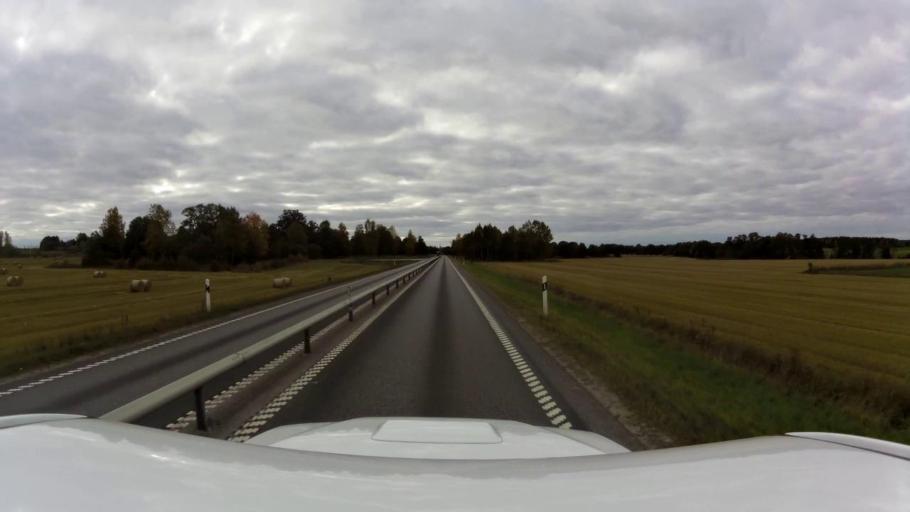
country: SE
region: OEstergoetland
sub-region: Linkopings Kommun
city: Malmslatt
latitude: 58.3671
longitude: 15.5443
